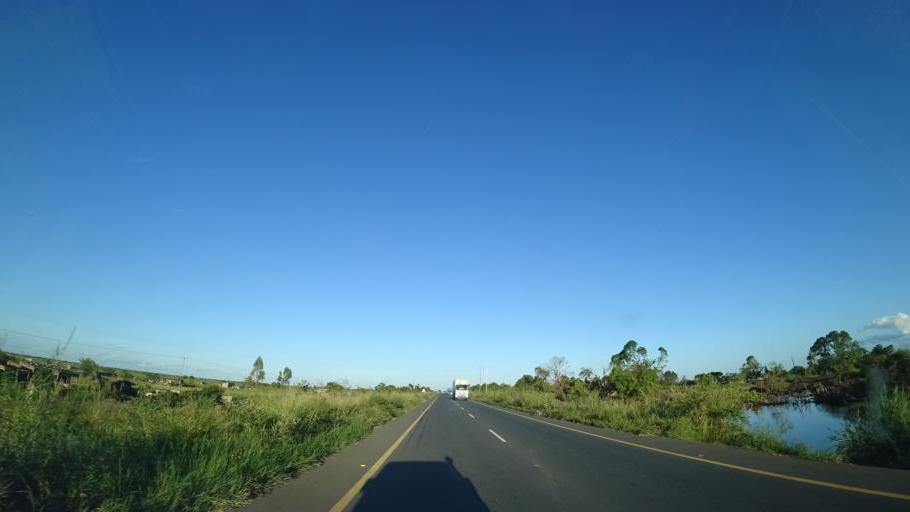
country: MZ
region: Sofala
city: Dondo
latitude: -19.3336
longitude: 34.3218
